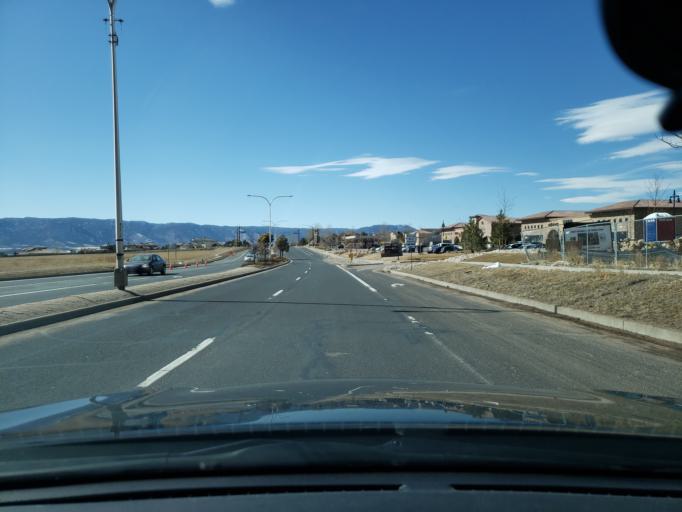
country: US
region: Colorado
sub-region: El Paso County
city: Gleneagle
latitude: 39.0288
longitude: -104.7788
